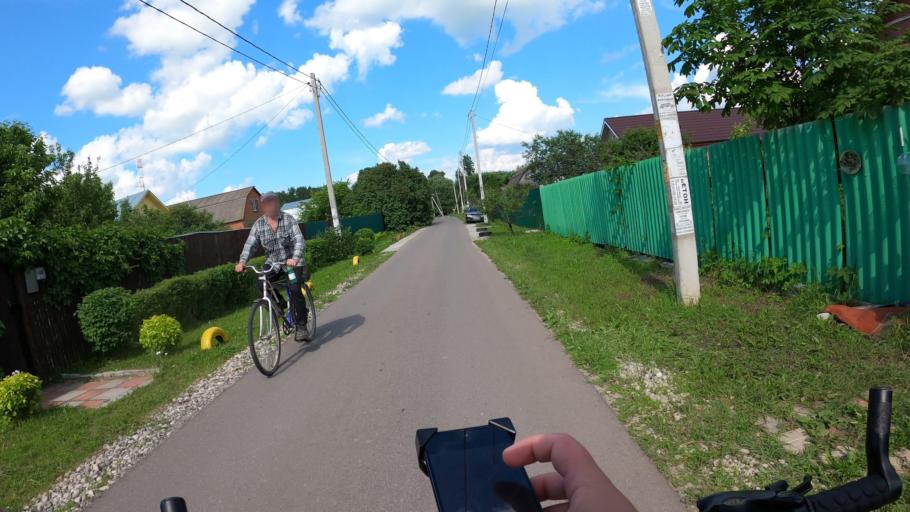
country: RU
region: Moskovskaya
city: Konobeyevo
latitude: 55.3957
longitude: 38.6765
